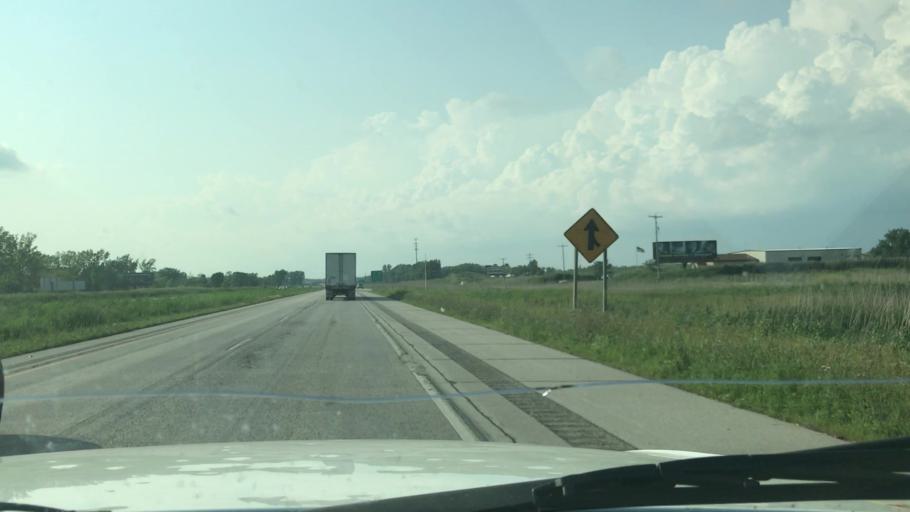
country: US
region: Wisconsin
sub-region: Brown County
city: Green Bay
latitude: 44.5426
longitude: -88.0289
